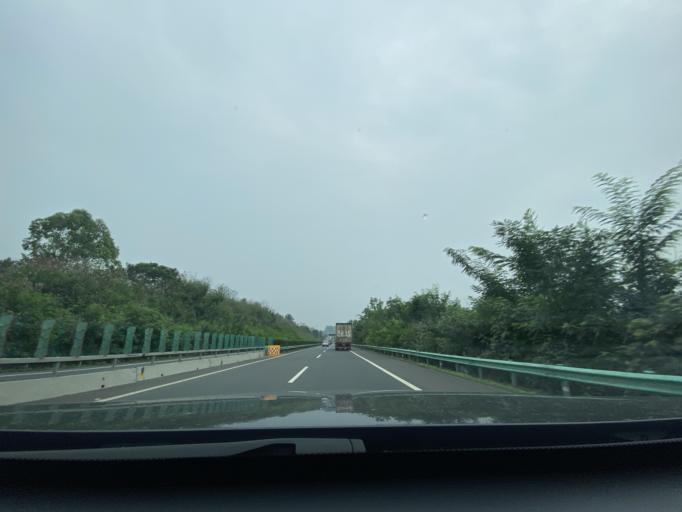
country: CN
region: Sichuan
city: Longquan
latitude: 30.3116
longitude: 104.1189
